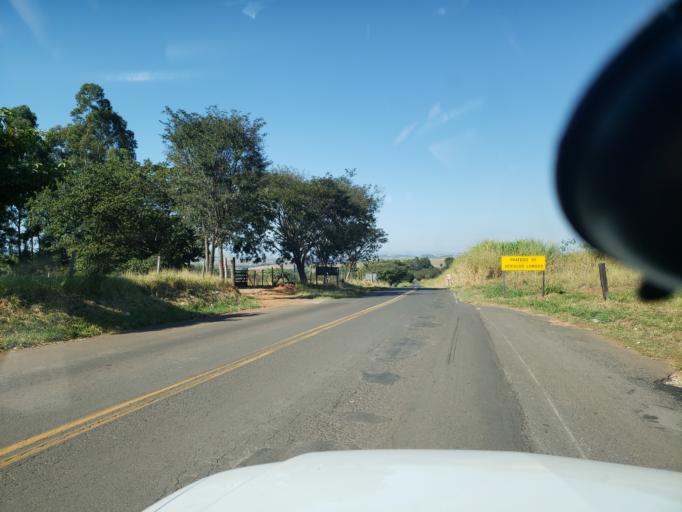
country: BR
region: Sao Paulo
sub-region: Moji-Guacu
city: Mogi-Gaucu
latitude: -22.3368
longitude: -46.8829
